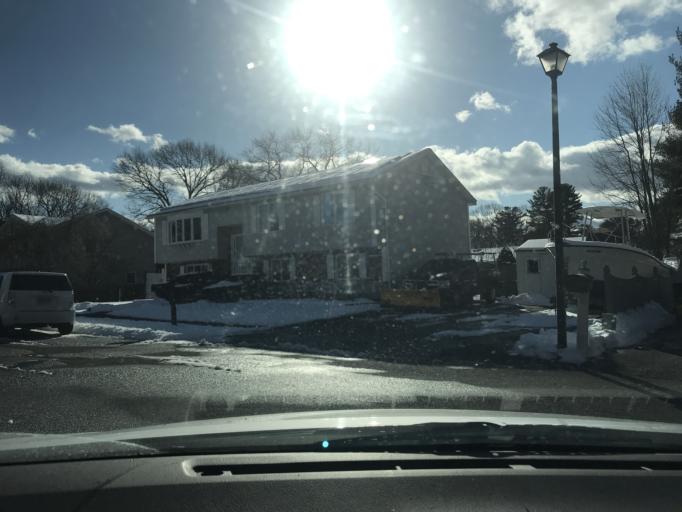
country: US
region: Massachusetts
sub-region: Essex County
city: Saugus
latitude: 42.4935
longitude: -71.0118
